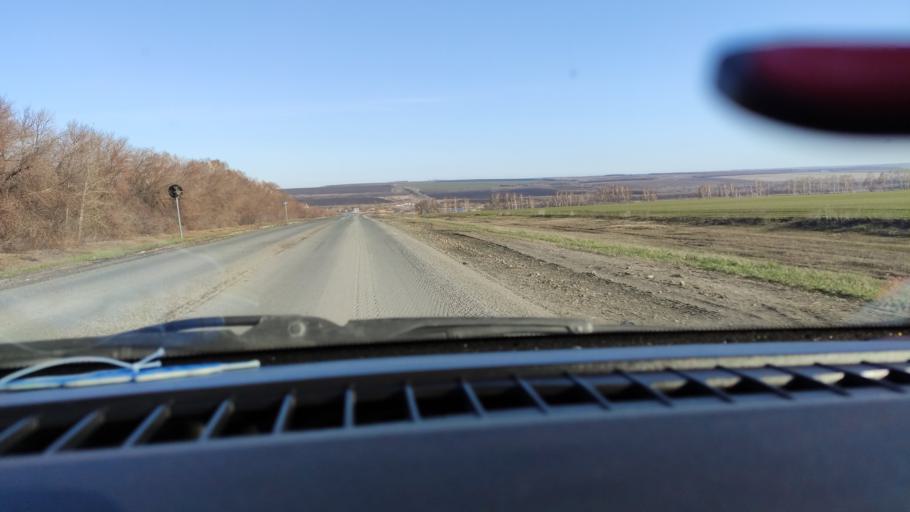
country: RU
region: Saratov
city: Dukhovnitskoye
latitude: 52.7238
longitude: 48.2620
